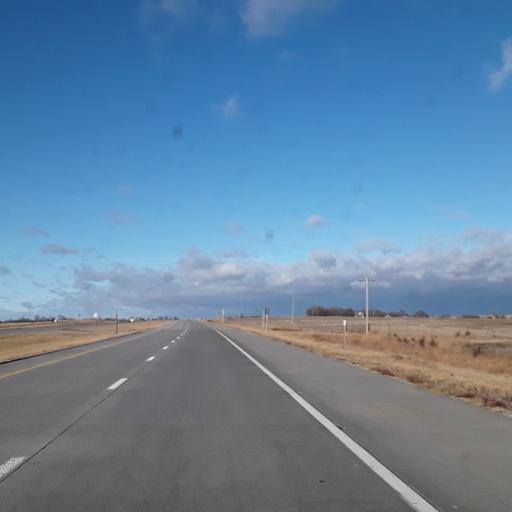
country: US
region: Kansas
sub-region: Republic County
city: Belleville
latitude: 39.8910
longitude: -97.6141
